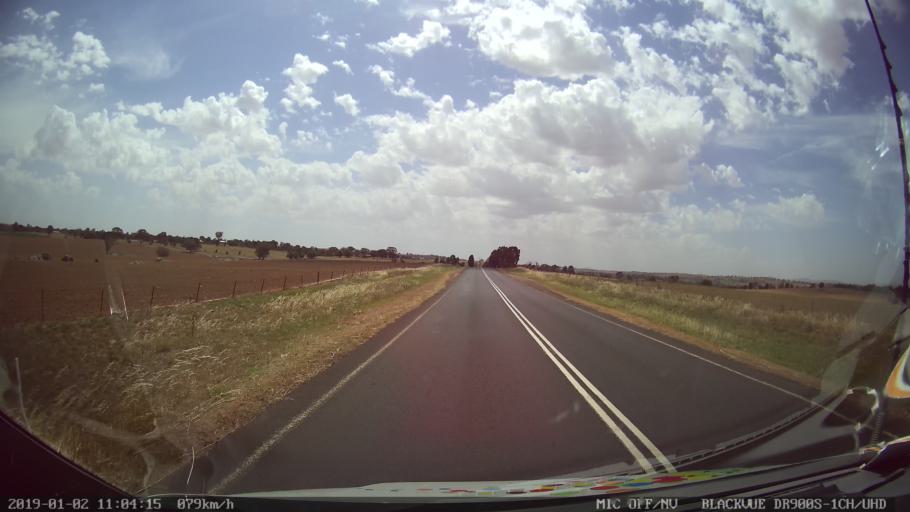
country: AU
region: New South Wales
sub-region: Young
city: Young
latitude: -34.5747
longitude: 148.3495
